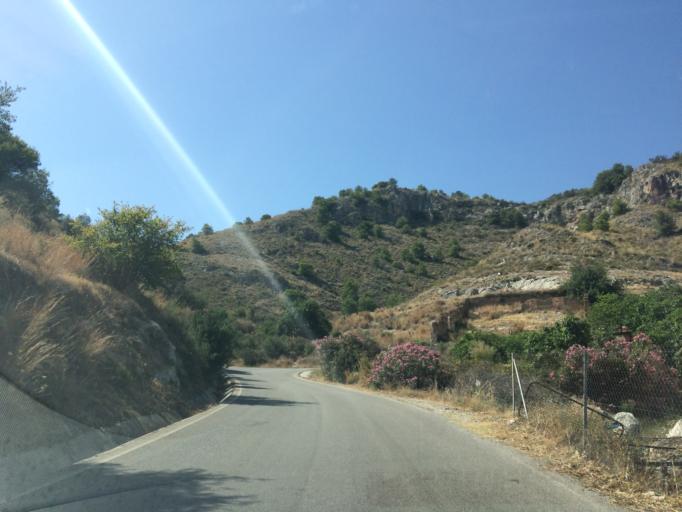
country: ES
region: Andalusia
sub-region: Provincia de Malaga
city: Frigiliana
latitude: 36.7969
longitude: -3.9017
